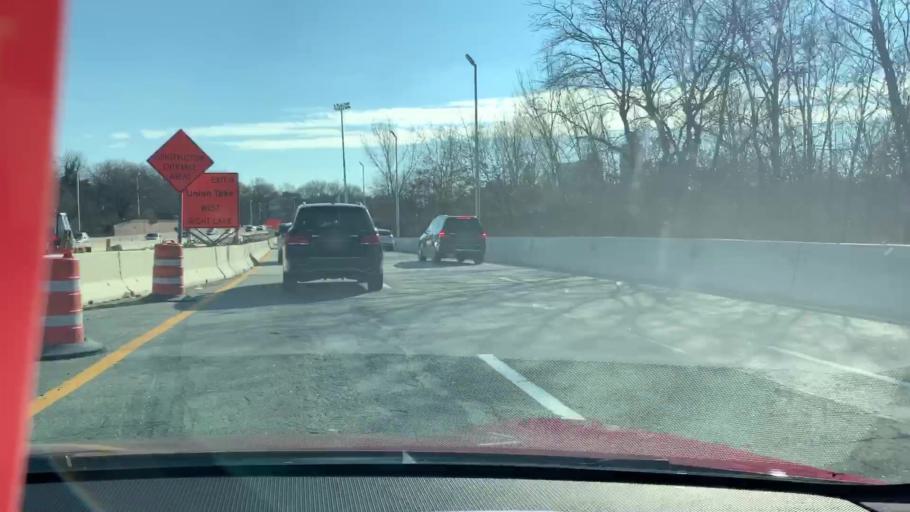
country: US
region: New York
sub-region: Queens County
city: Jamaica
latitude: 40.7224
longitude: -73.8275
